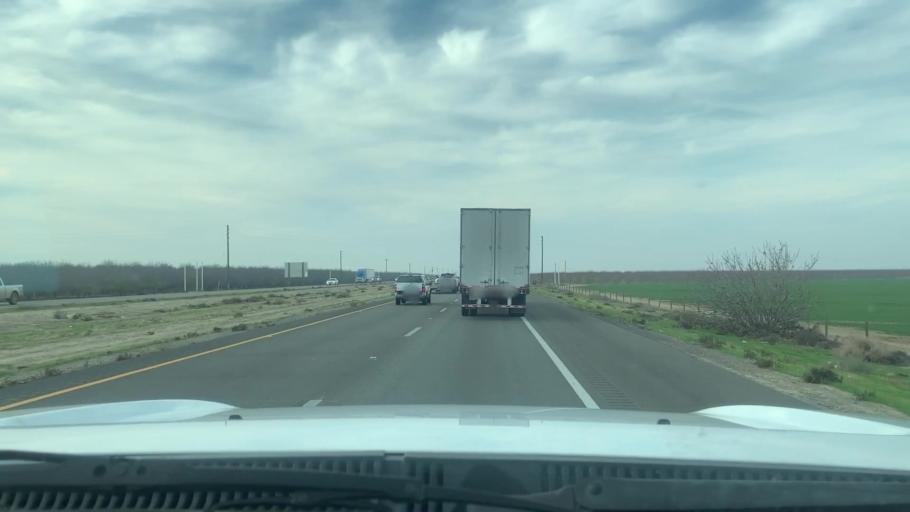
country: US
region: California
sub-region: Kern County
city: Buttonwillow
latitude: 35.4609
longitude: -119.4822
